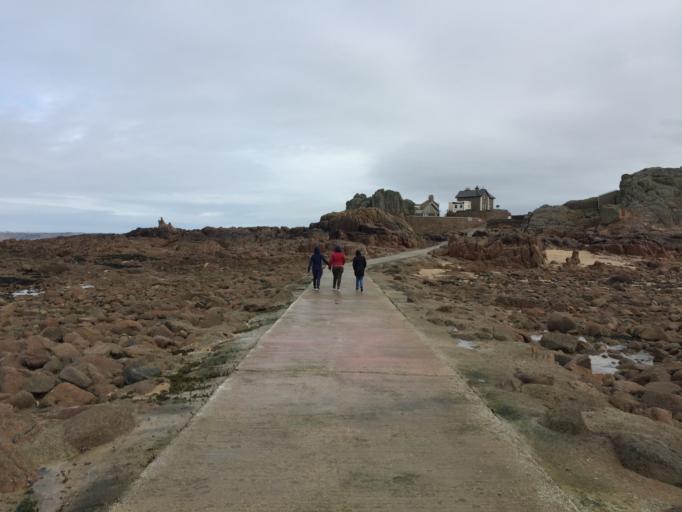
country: JE
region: St Helier
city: Saint Helier
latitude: 49.1812
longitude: -2.2463
